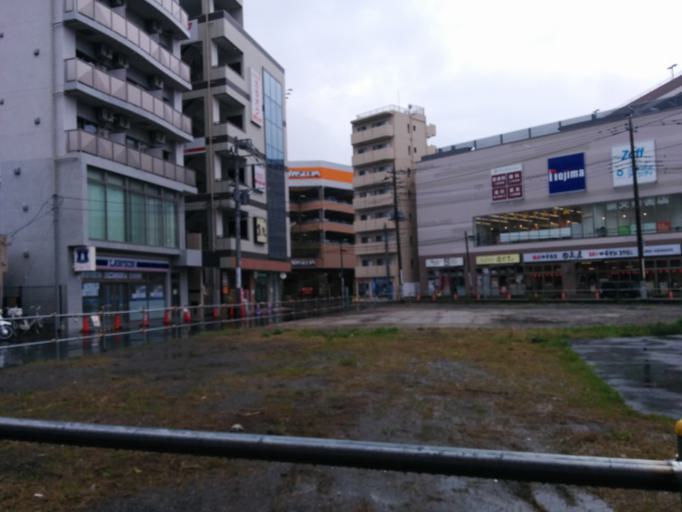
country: JP
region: Saitama
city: Shimotoda
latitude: 35.8175
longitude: 139.6694
